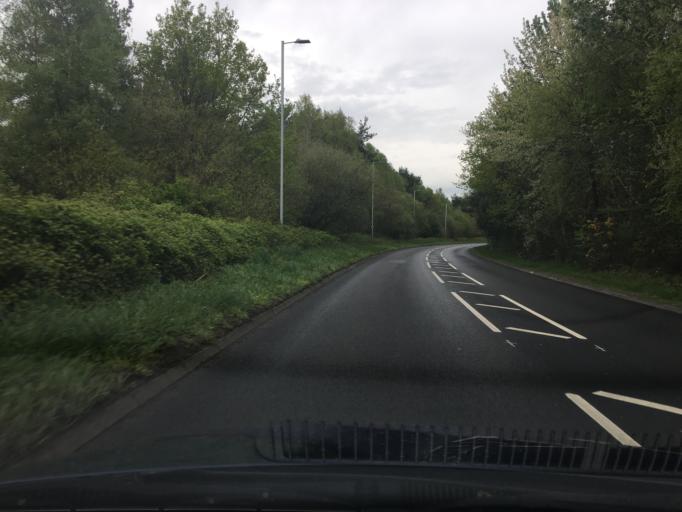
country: GB
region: England
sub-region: Bracknell Forest
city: Sandhurst
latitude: 51.3539
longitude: -0.7884
